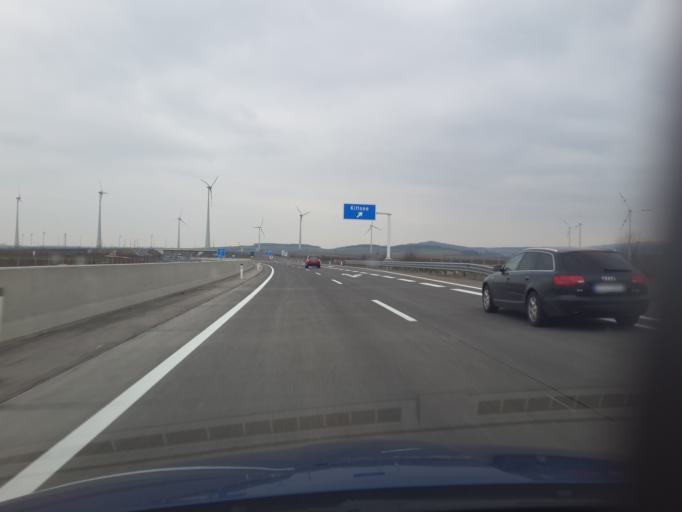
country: AT
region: Lower Austria
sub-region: Politischer Bezirk Bruck an der Leitha
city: Berg
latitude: 48.0820
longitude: 17.0386
